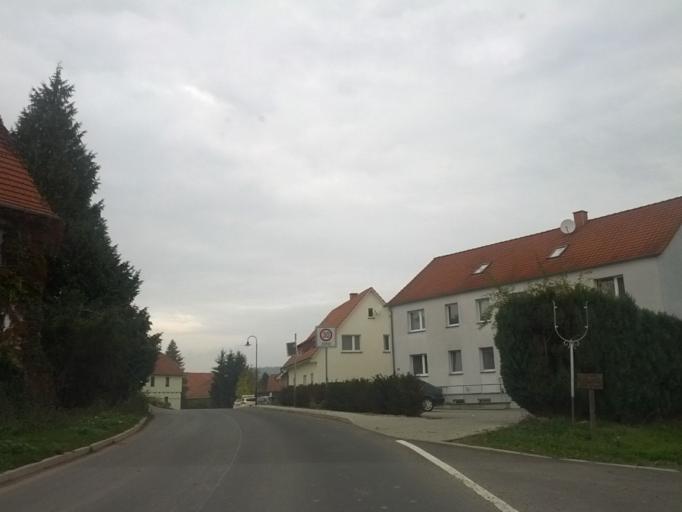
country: DE
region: Thuringia
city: Creuzburg
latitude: 51.0214
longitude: 10.2264
